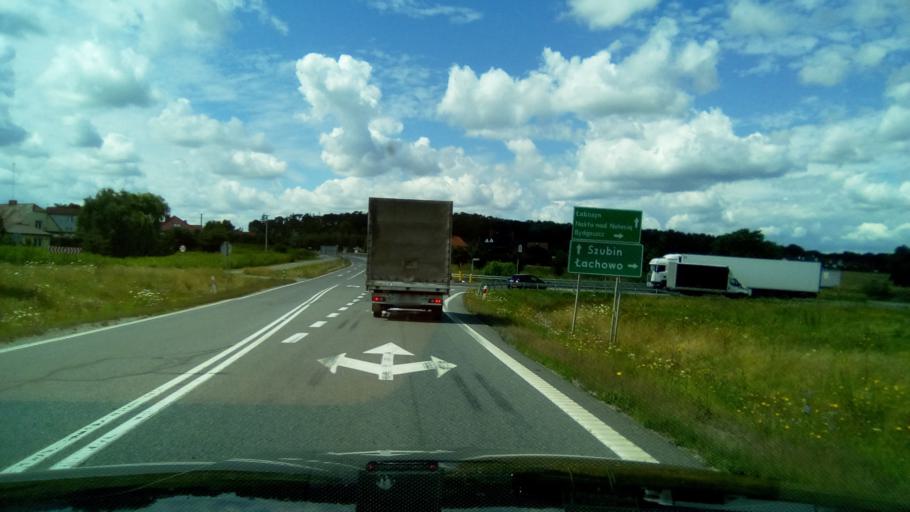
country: PL
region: Kujawsko-Pomorskie
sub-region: Powiat nakielski
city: Szubin
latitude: 53.0190
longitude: 17.7634
